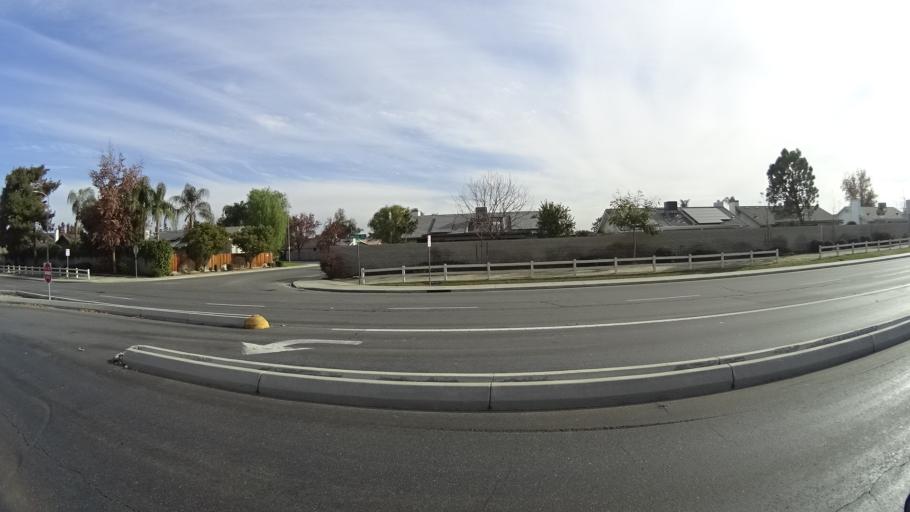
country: US
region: California
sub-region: Kern County
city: Rosedale
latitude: 35.4068
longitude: -119.1279
